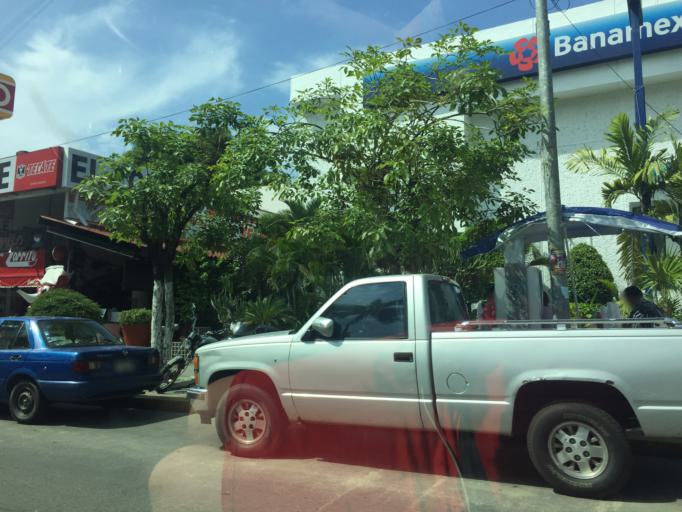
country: MX
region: Guerrero
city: Acapulco de Juarez
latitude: 16.8614
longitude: -99.8797
